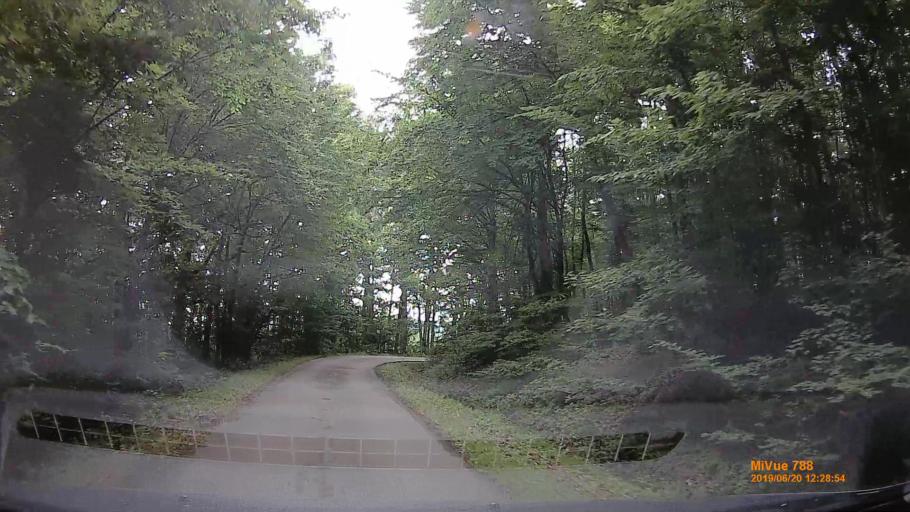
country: HU
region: Baranya
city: Hosszuheteny
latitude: 46.2044
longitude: 18.3512
